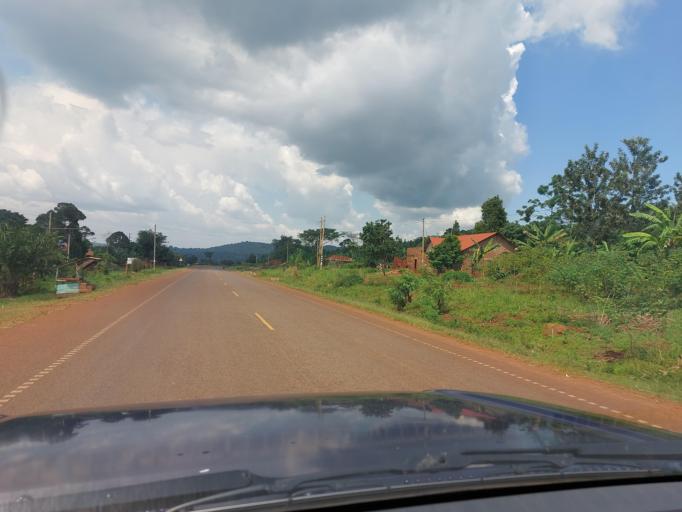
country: UG
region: Central Region
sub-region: Buikwe District
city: Njeru
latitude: 0.3327
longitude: 33.1198
